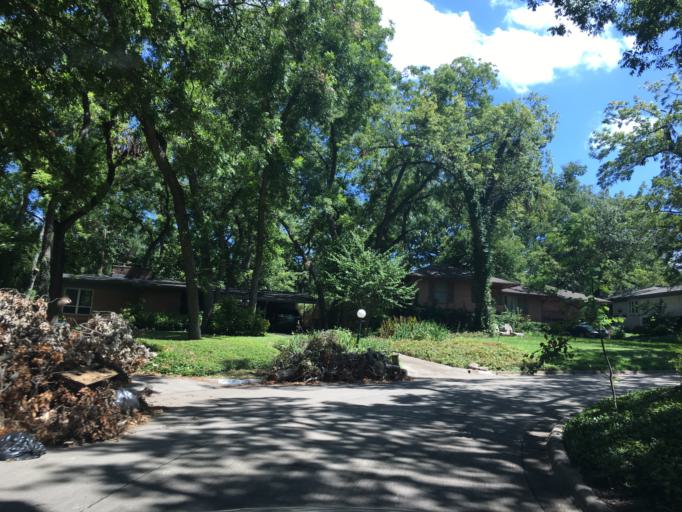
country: US
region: Texas
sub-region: Dallas County
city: Garland
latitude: 32.8445
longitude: -96.6991
